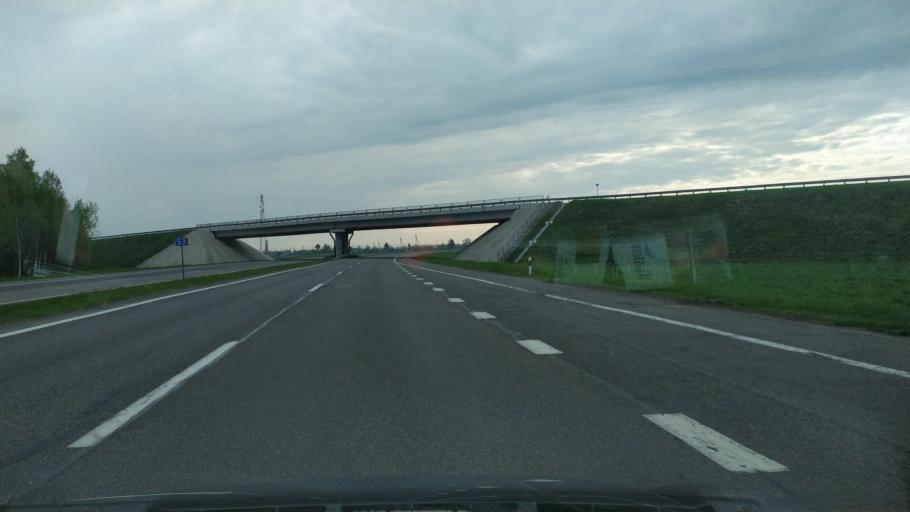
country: BY
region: Brest
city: Kobryn
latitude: 52.2023
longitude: 24.2812
